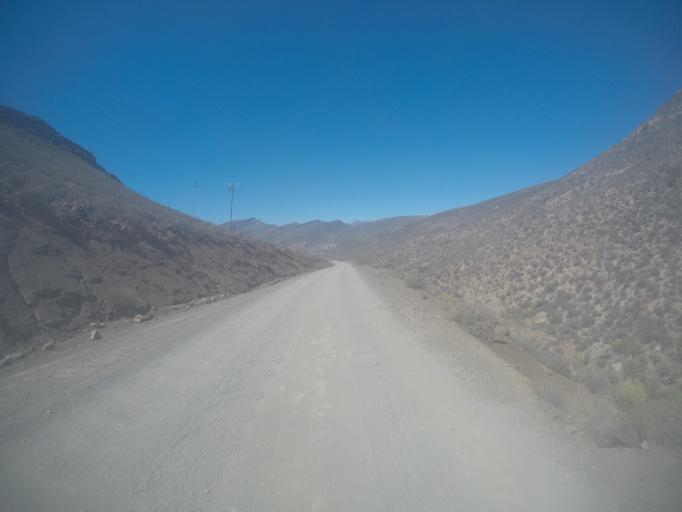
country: ZA
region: Western Cape
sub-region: West Coast District Municipality
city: Clanwilliam
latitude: -32.5389
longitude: 19.3562
